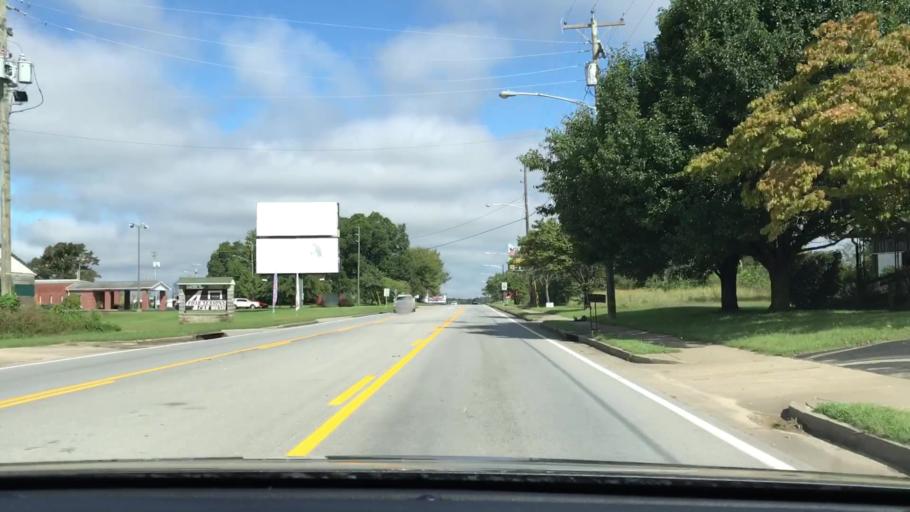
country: US
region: Kentucky
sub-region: Russell County
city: Jamestown
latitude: 37.0030
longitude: -85.0735
